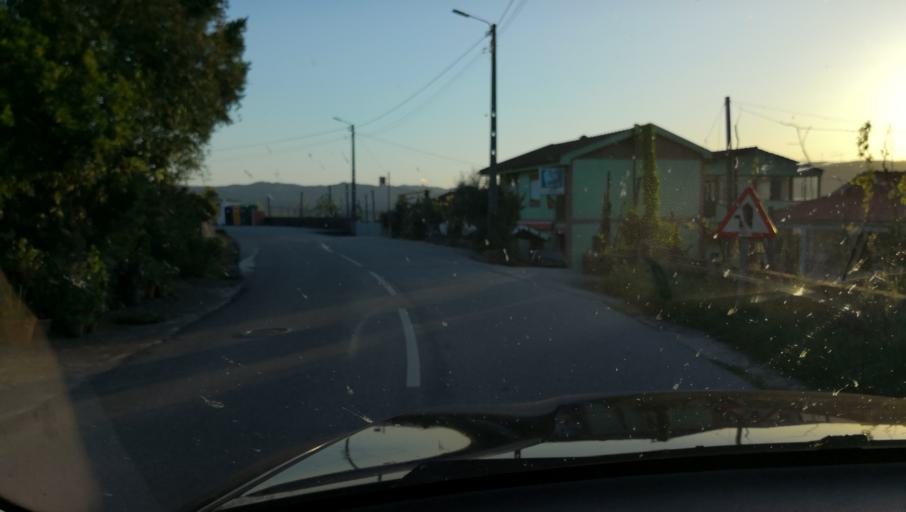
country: PT
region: Vila Real
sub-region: Mondim de Basto
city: Mondim de Basto
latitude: 41.4110
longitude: -7.9445
